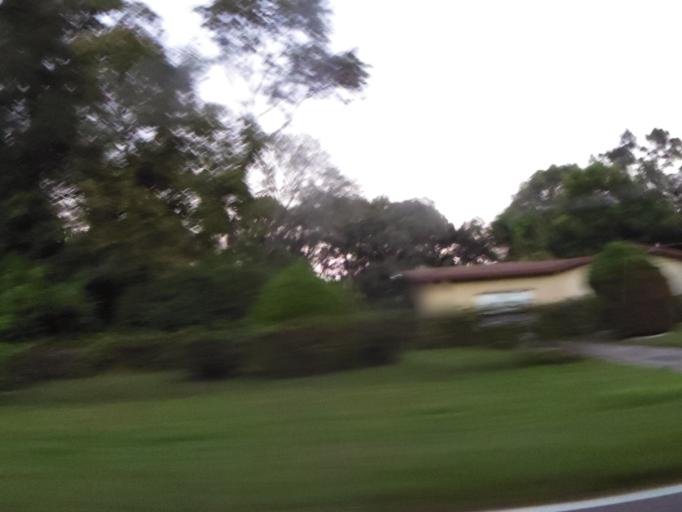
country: US
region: Florida
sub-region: Duval County
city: Jacksonville
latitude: 30.2930
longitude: -81.7220
